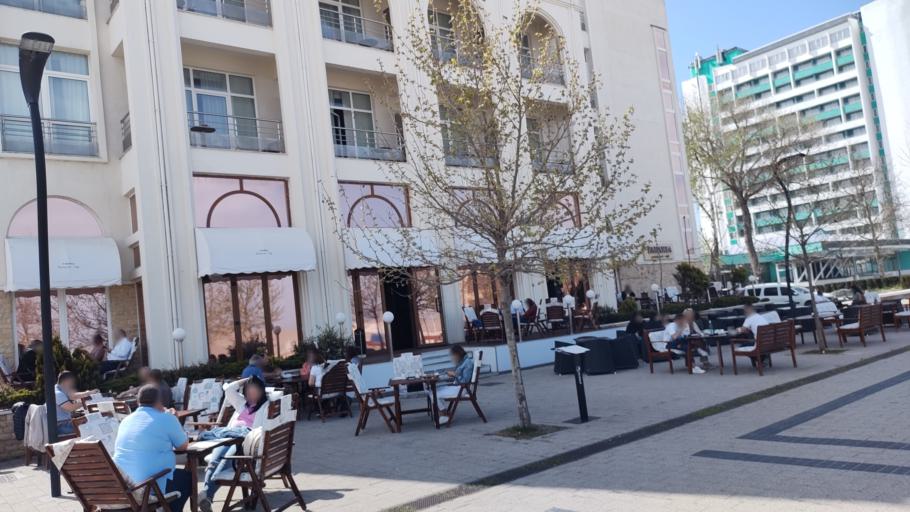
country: RO
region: Constanta
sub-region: Municipiul Constanta
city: Palazu Mare
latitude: 44.2440
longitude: 28.6229
